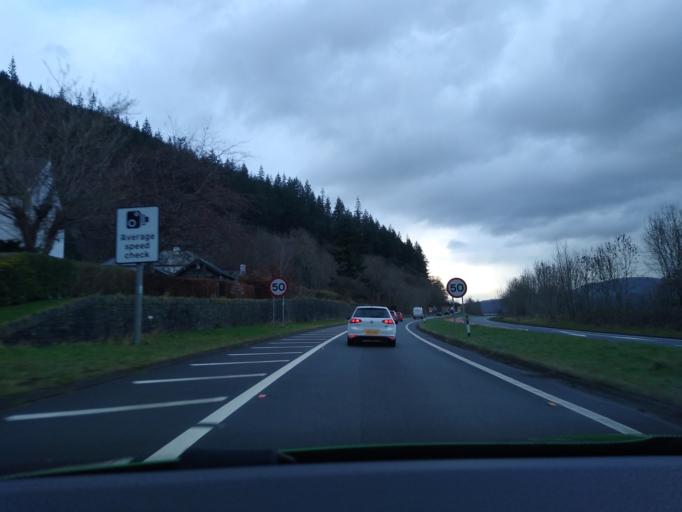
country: GB
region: England
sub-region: Cumbria
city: Keswick
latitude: 54.6441
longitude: -3.2183
